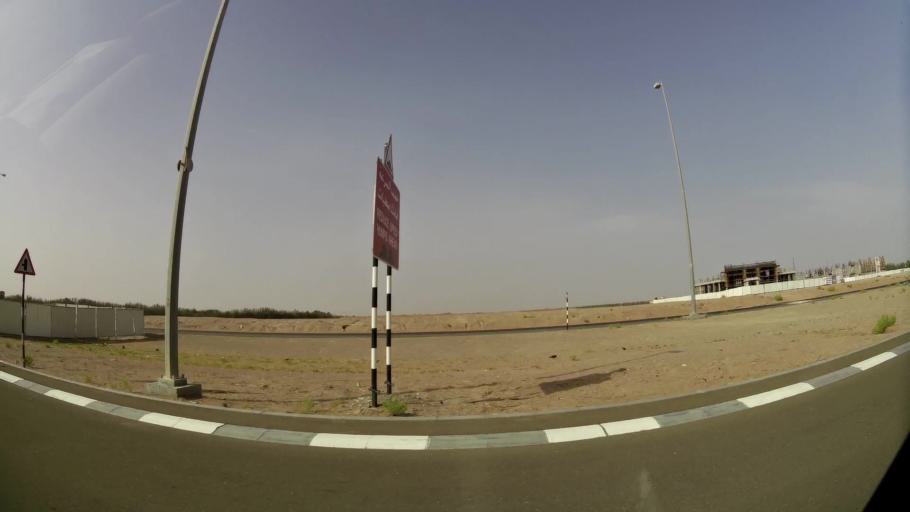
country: AE
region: Abu Dhabi
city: Al Ain
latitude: 24.2107
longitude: 55.5993
